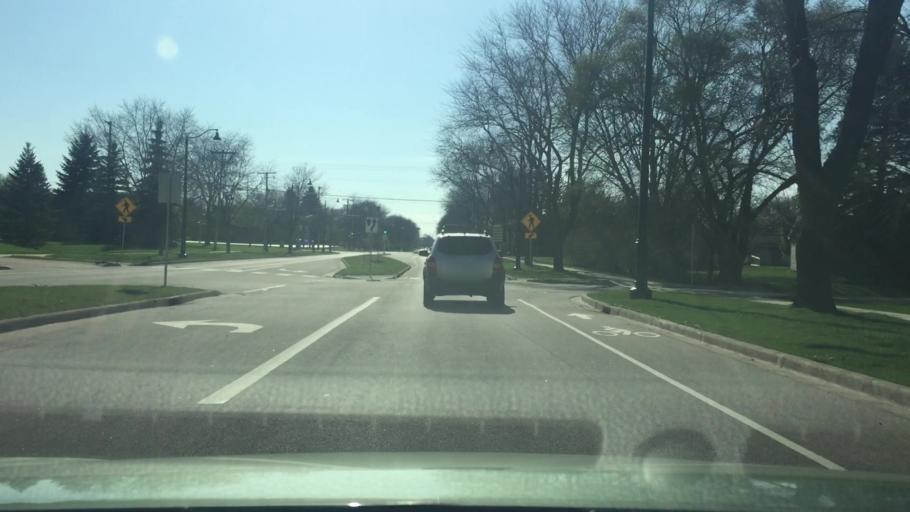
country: US
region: Wisconsin
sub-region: Milwaukee County
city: Brown Deer
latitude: 43.1632
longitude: -87.9730
